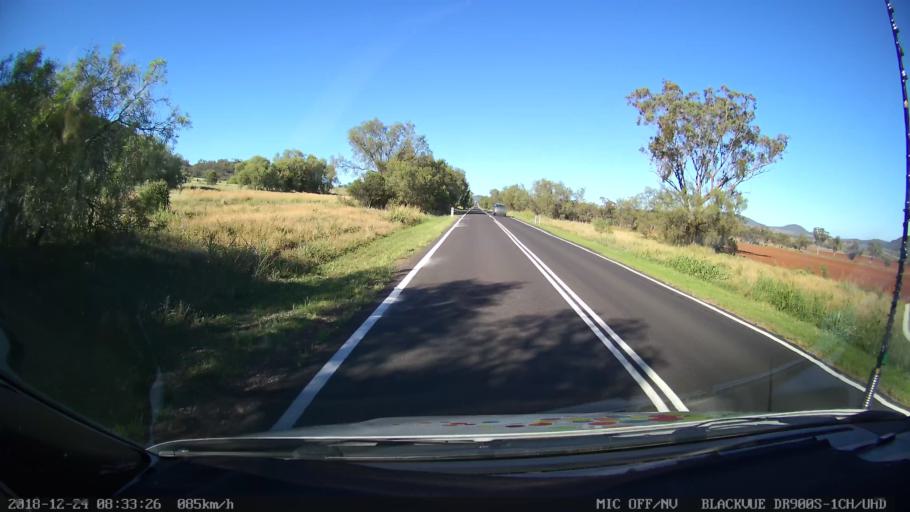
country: AU
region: New South Wales
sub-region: Liverpool Plains
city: Quirindi
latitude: -31.2863
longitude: 150.6846
